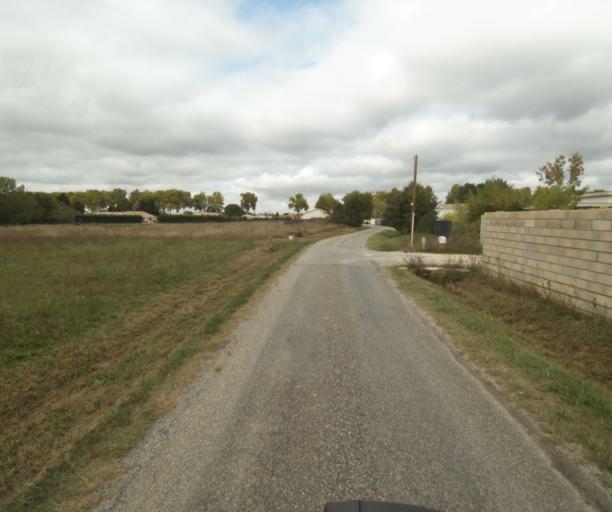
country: FR
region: Midi-Pyrenees
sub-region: Departement du Tarn-et-Garonne
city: Montech
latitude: 43.9623
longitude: 1.2539
